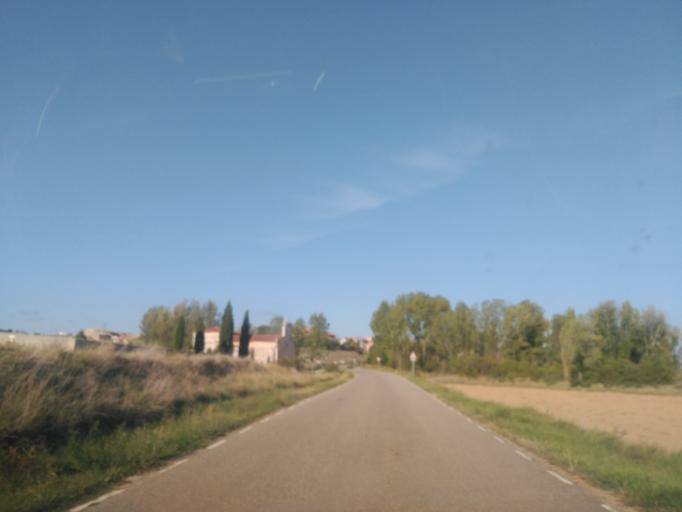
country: ES
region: Castille and Leon
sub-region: Provincia de Burgos
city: Brazacorta
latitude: 41.7145
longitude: -3.3698
